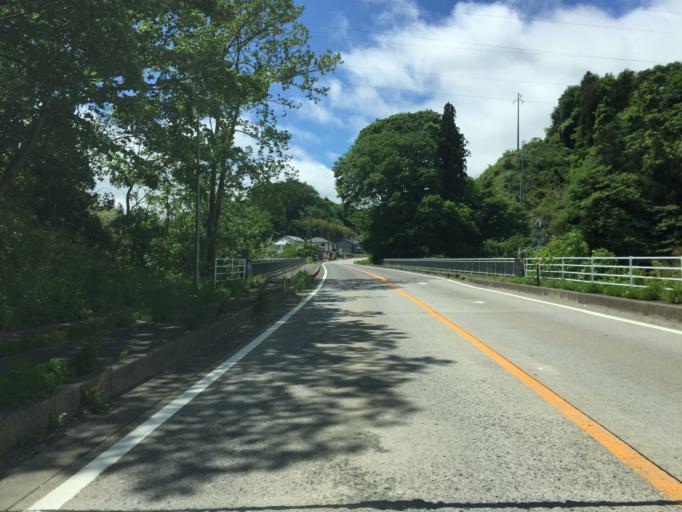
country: JP
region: Fukushima
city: Miharu
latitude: 37.4391
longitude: 140.5024
